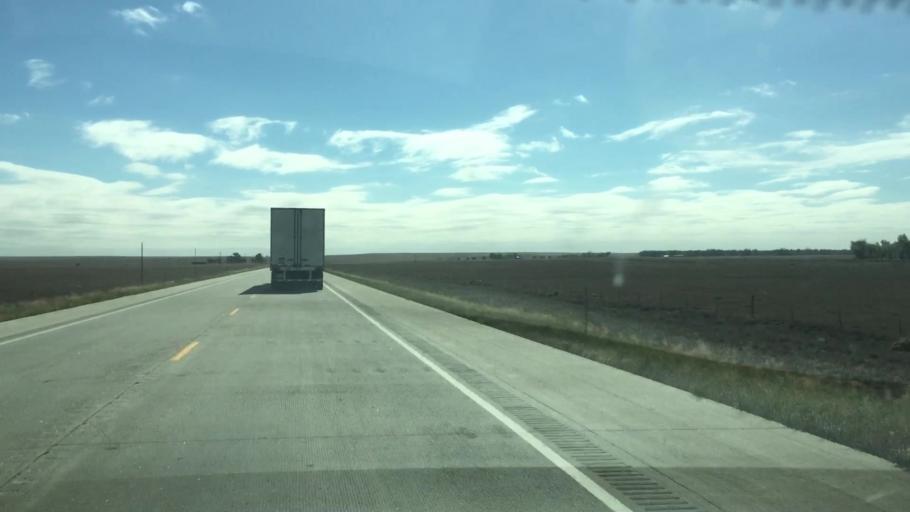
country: US
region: Colorado
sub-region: Lincoln County
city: Hugo
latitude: 39.0591
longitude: -103.3603
